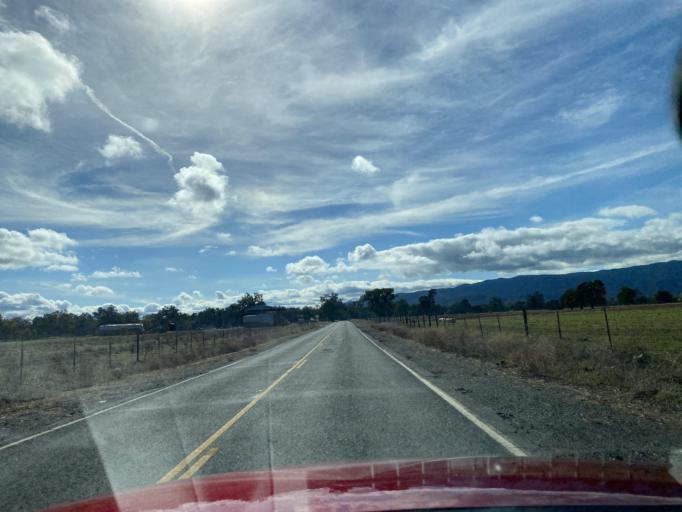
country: US
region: California
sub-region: Glenn County
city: Willows
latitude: 39.4027
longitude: -122.5518
